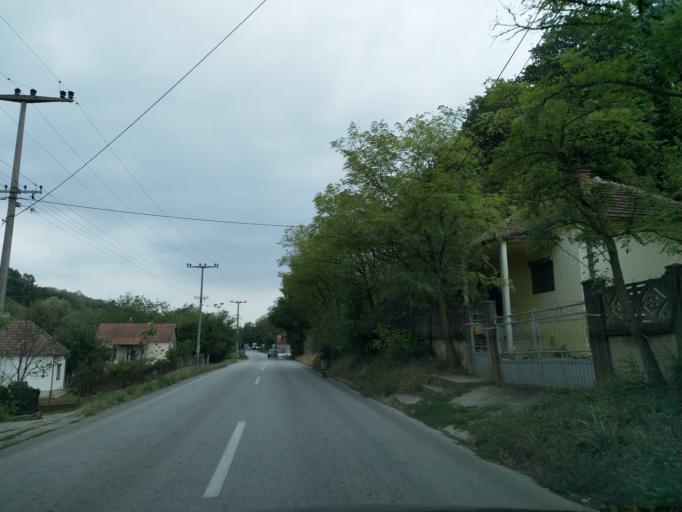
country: RS
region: Central Serbia
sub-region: Pomoravski Okrug
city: Jagodina
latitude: 44.0432
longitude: 21.1858
